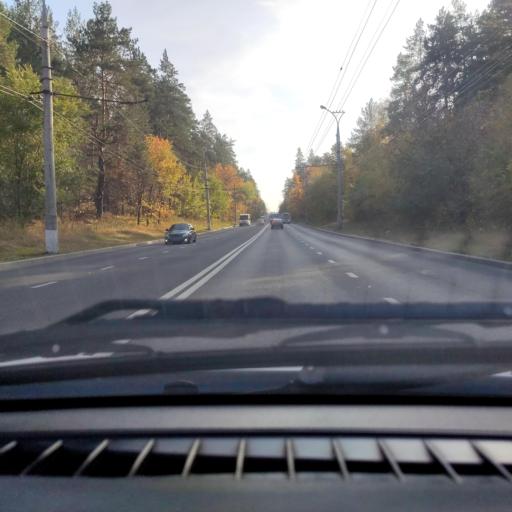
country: RU
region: Samara
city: Zhigulevsk
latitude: 53.4998
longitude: 49.4633
